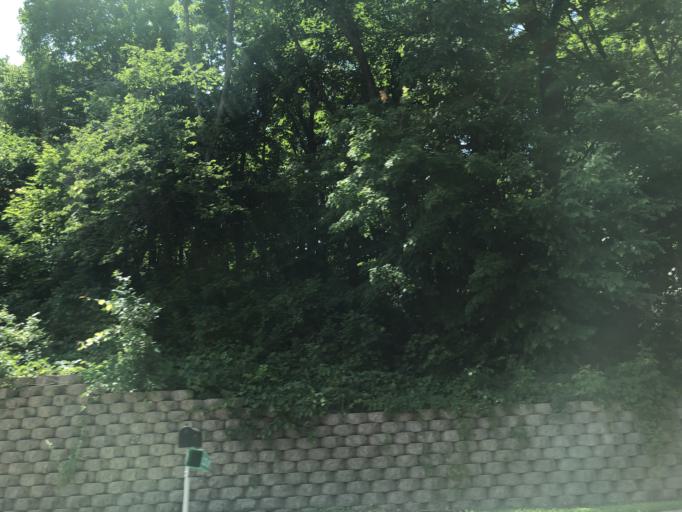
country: US
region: Minnesota
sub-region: Douglas County
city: Alexandria
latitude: 45.9338
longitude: -95.3836
